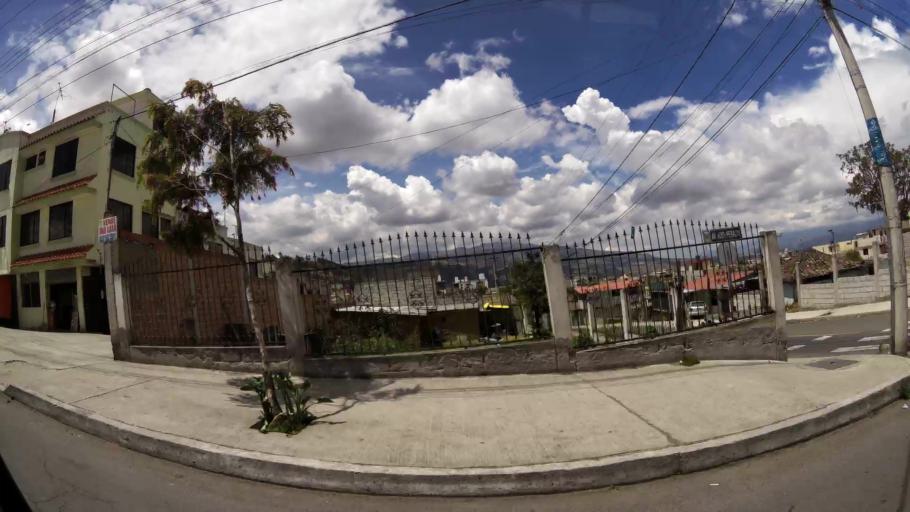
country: EC
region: Tungurahua
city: Ambato
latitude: -1.2793
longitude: -78.6368
